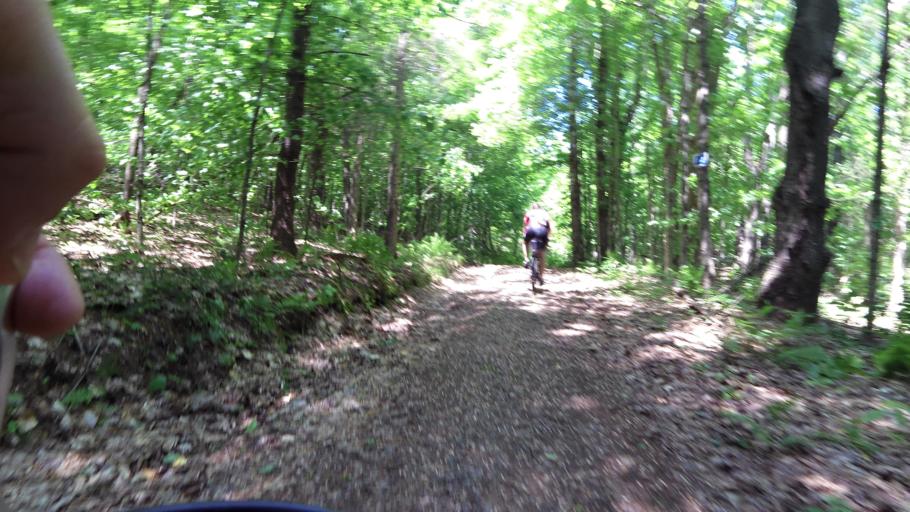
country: CA
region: Quebec
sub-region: Outaouais
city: Wakefield
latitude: 45.5836
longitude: -75.9648
